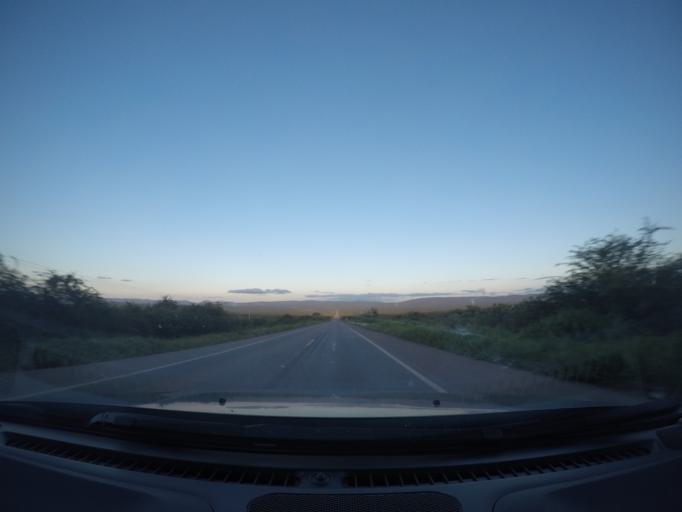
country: BR
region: Bahia
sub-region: Seabra
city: Seabra
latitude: -12.4108
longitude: -41.9704
